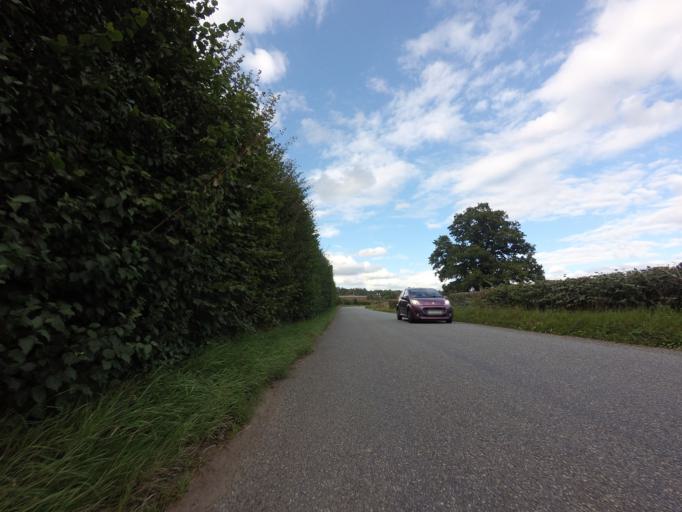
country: GB
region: England
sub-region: Kent
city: Marden
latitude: 51.2109
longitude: 0.5076
